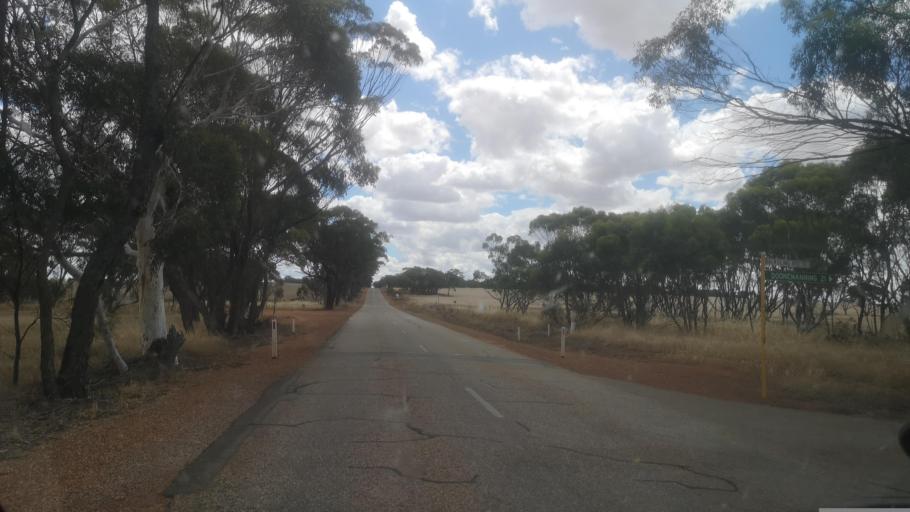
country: AU
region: Western Australia
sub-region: Beverley
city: Beverley
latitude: -31.9899
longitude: 117.1216
